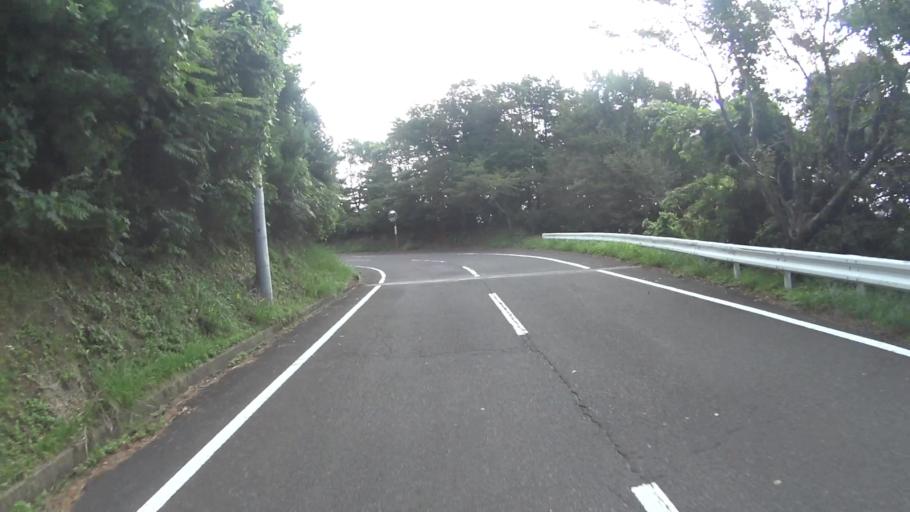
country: JP
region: Kyoto
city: Miyazu
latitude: 35.7329
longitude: 135.1770
